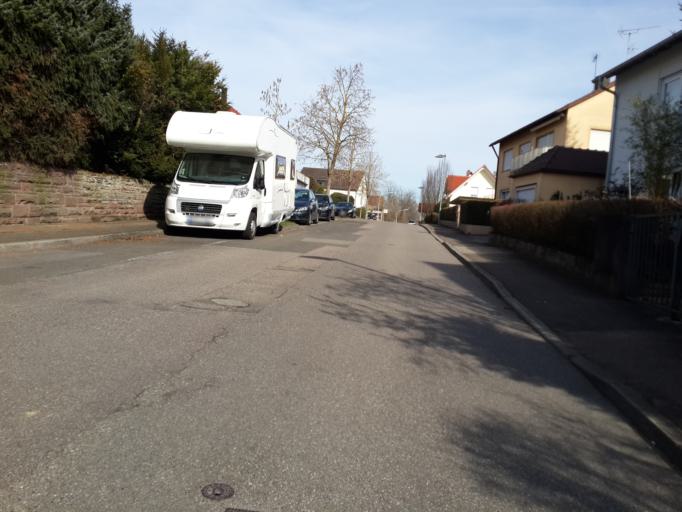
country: DE
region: Baden-Wuerttemberg
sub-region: Regierungsbezirk Stuttgart
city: Heilbronn
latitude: 49.1423
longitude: 9.1860
